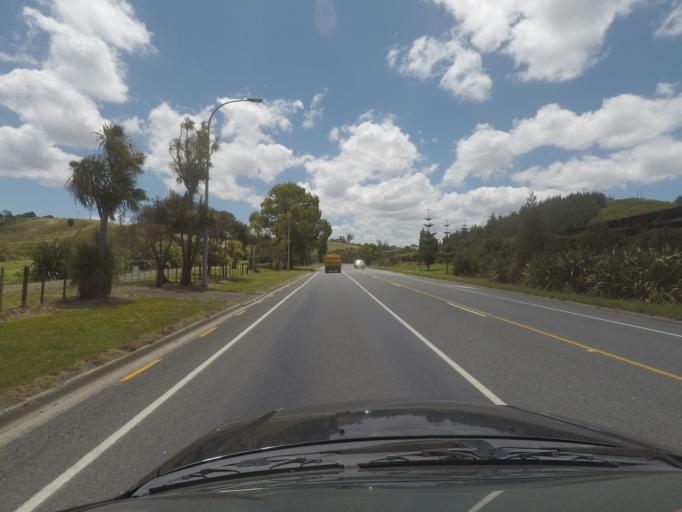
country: NZ
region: Northland
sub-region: Whangarei
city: Whangarei
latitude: -35.7504
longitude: 174.3205
